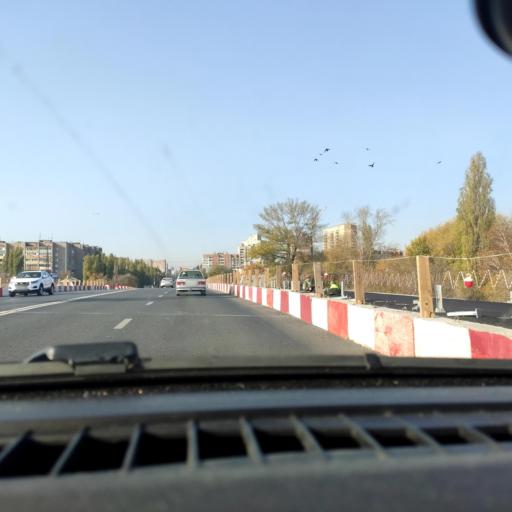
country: RU
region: Voronezj
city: Voronezh
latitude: 51.6679
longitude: 39.1701
